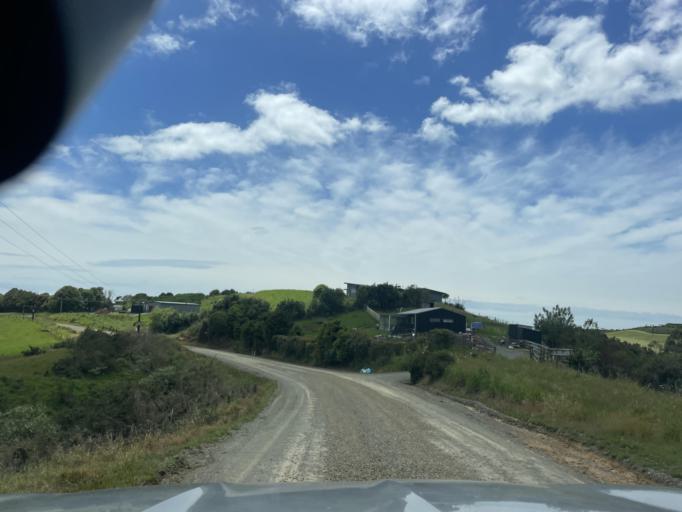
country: NZ
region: Auckland
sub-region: Auckland
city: Wellsford
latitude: -36.1566
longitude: 174.5413
